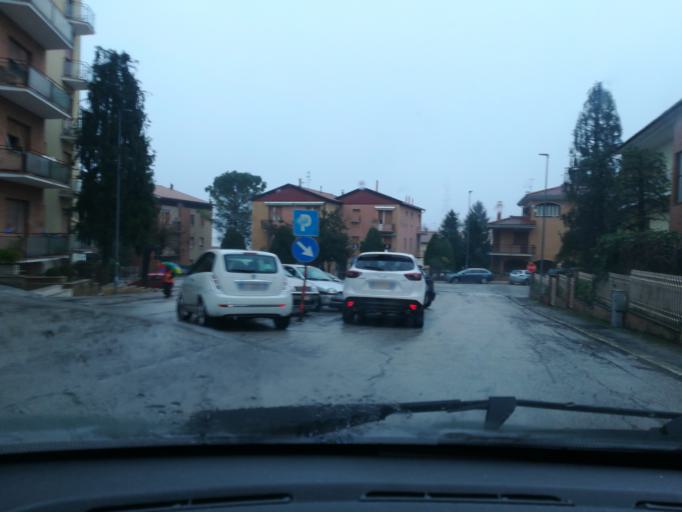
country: IT
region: The Marches
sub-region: Provincia di Macerata
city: Villa Potenza
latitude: 43.2985
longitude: 13.4295
